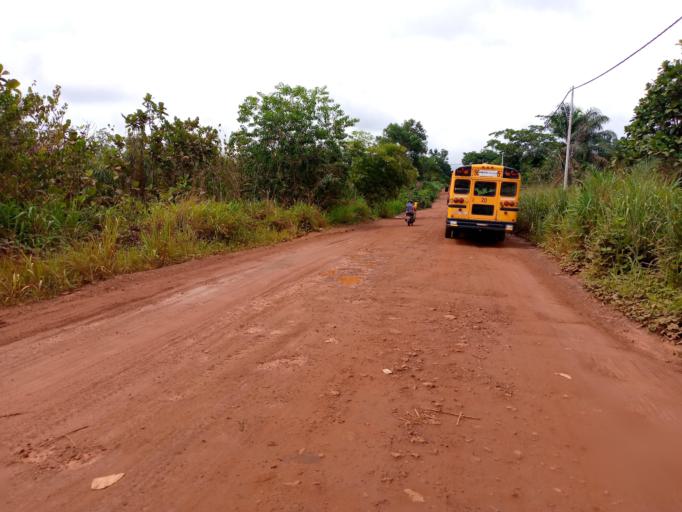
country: SL
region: Southern Province
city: Mogbwemo
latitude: 7.7724
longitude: -12.2964
